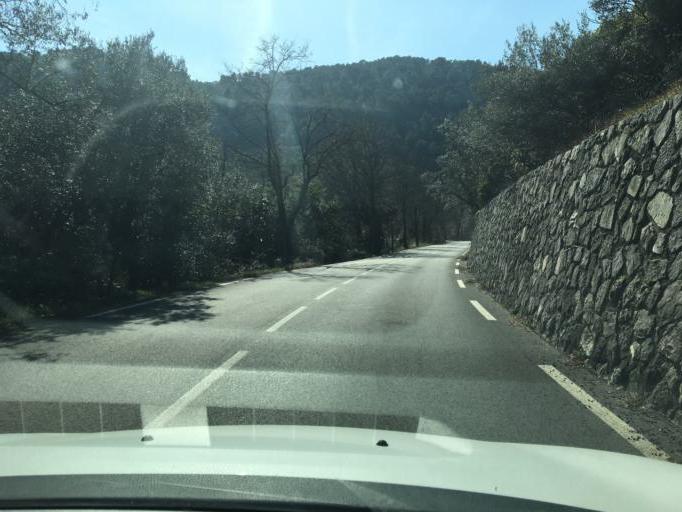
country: FR
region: Provence-Alpes-Cote d'Azur
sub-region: Departement du Var
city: Bargemon
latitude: 43.6167
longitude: 6.5416
